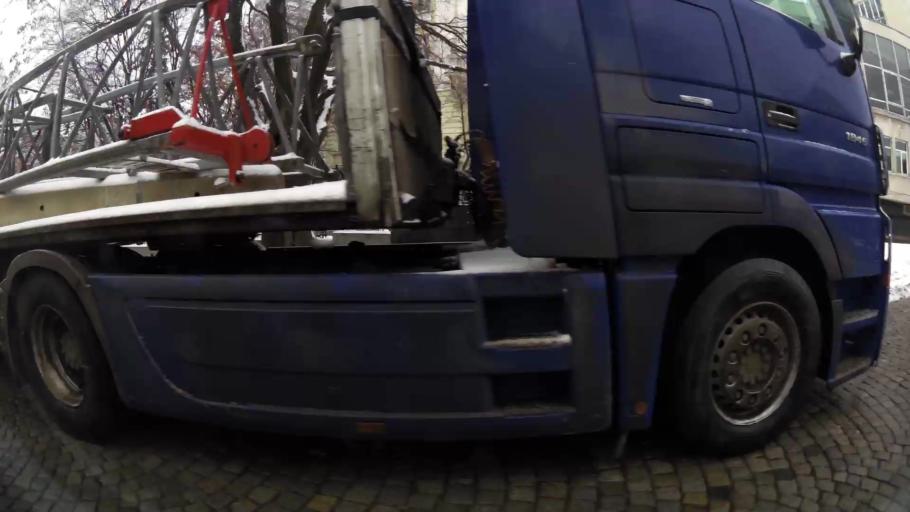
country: BG
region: Sofia-Capital
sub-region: Stolichna Obshtina
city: Sofia
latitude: 42.6965
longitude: 23.3148
